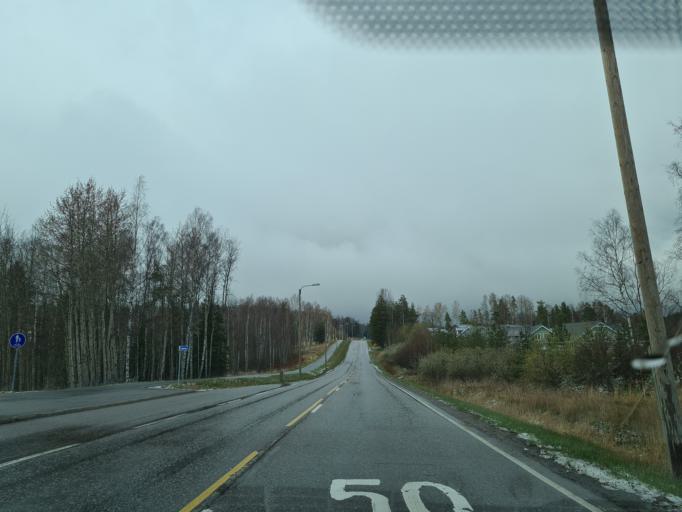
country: FI
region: Uusimaa
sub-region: Helsinki
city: Kirkkonummi
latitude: 60.0875
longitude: 24.4087
